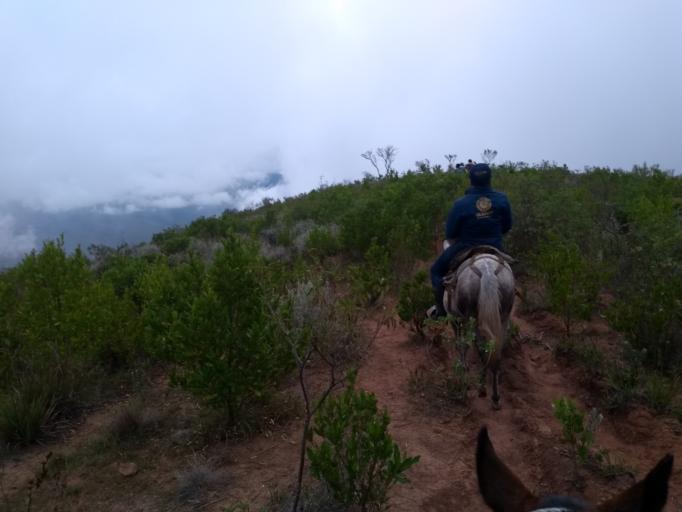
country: CO
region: Cesar
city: Manaure Balcon del Cesar
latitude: 10.2047
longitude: -73.0033
